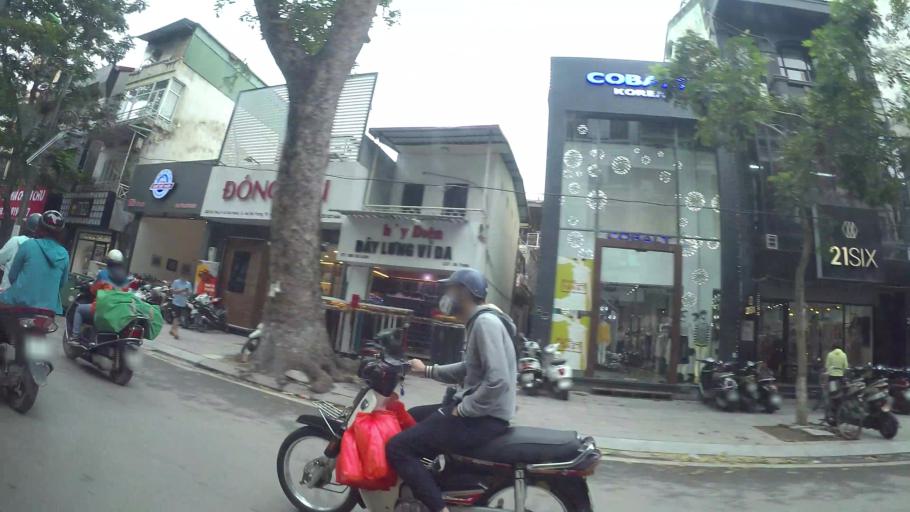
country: VN
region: Ha Noi
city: Hai BaTrung
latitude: 21.0149
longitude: 105.8492
